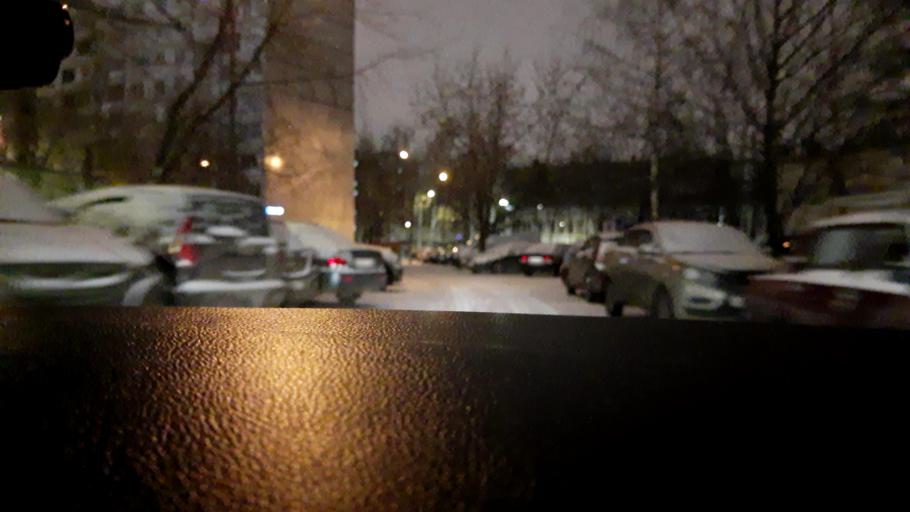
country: RU
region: Moskovskaya
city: Razvilka
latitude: 55.6013
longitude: 37.7444
